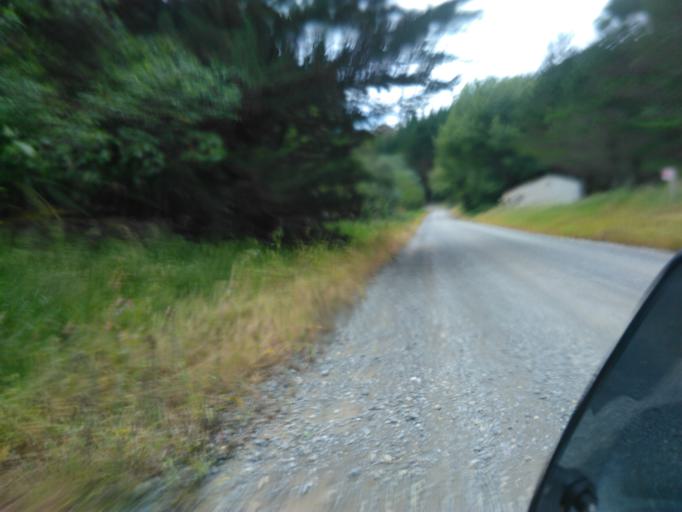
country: NZ
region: Gisborne
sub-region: Gisborne District
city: Gisborne
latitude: -38.0550
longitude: 178.1330
